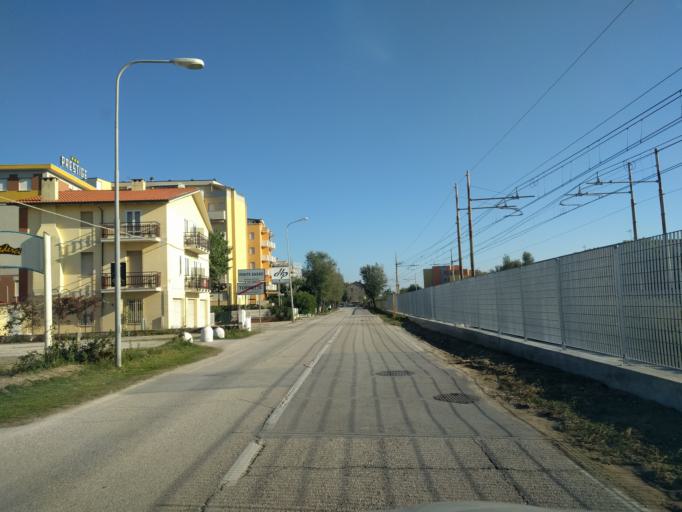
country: IT
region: The Marches
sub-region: Provincia di Pesaro e Urbino
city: Marotta
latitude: 43.7897
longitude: 13.1078
